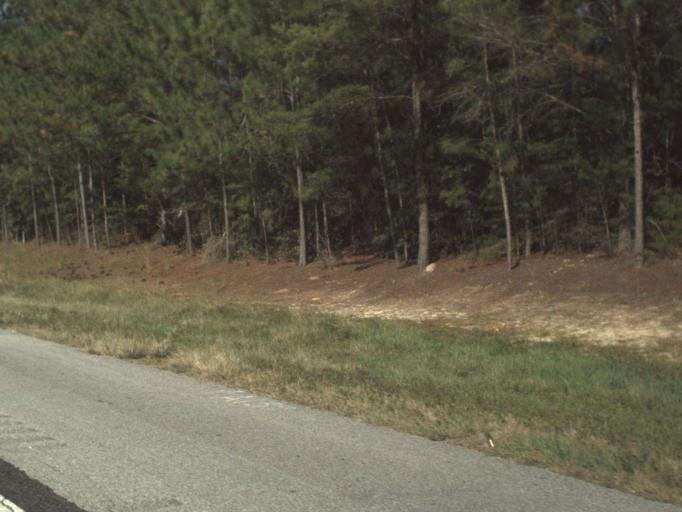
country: US
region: Florida
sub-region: Okaloosa County
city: Crestview
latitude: 30.7306
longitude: -86.3881
